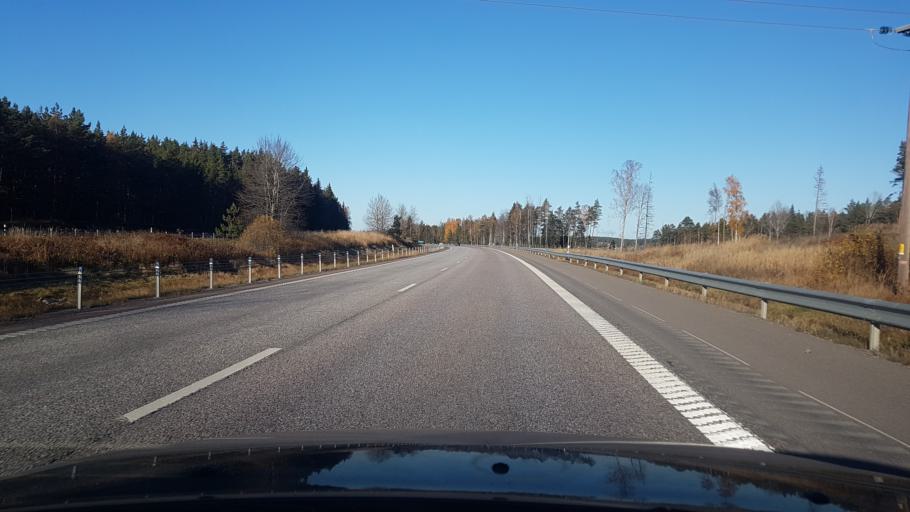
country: SE
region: Uppsala
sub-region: Uppsala Kommun
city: Alsike
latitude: 59.7943
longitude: 17.7736
